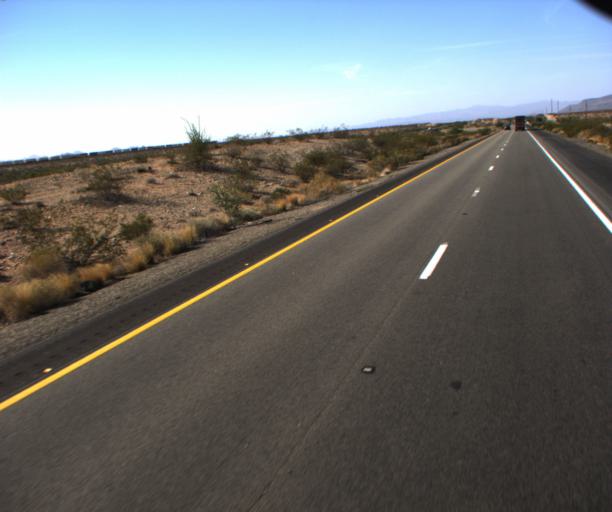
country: US
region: Arizona
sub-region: Mohave County
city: Kingman
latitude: 34.9675
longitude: -114.1432
